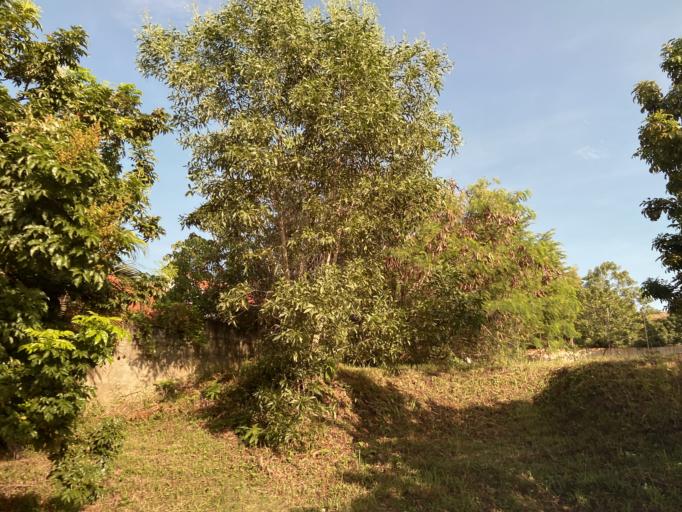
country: SG
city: Singapore
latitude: 1.0963
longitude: 104.0297
